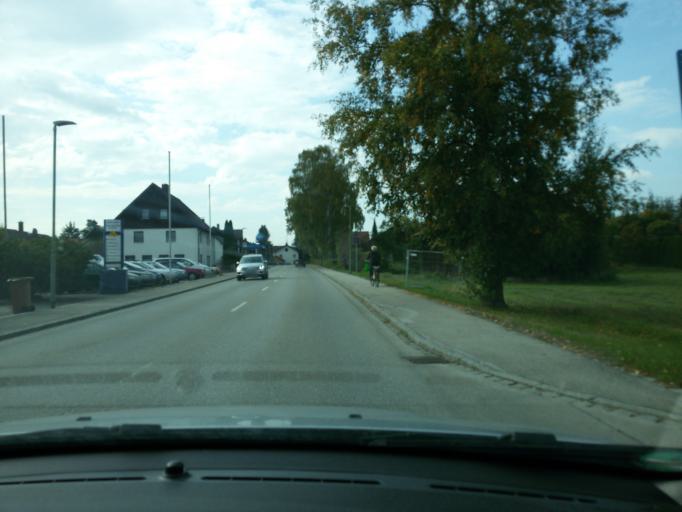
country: DE
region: Bavaria
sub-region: Swabia
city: Buchloe
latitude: 48.0360
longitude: 10.7343
